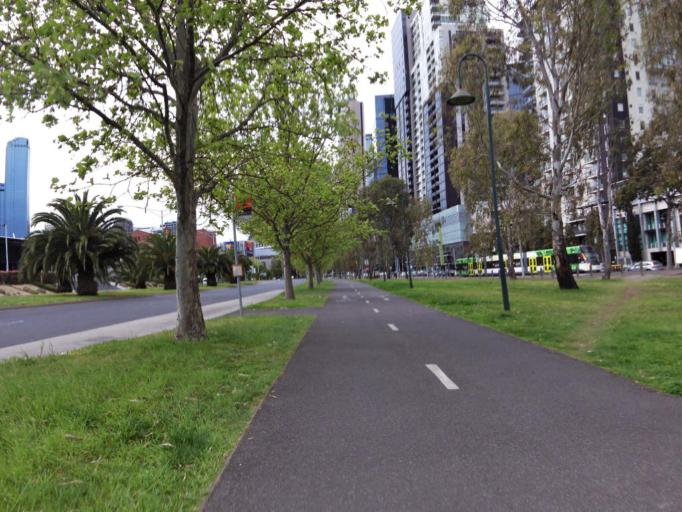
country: AU
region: Victoria
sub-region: Melbourne
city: Southbank
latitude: -37.8267
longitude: 144.9549
